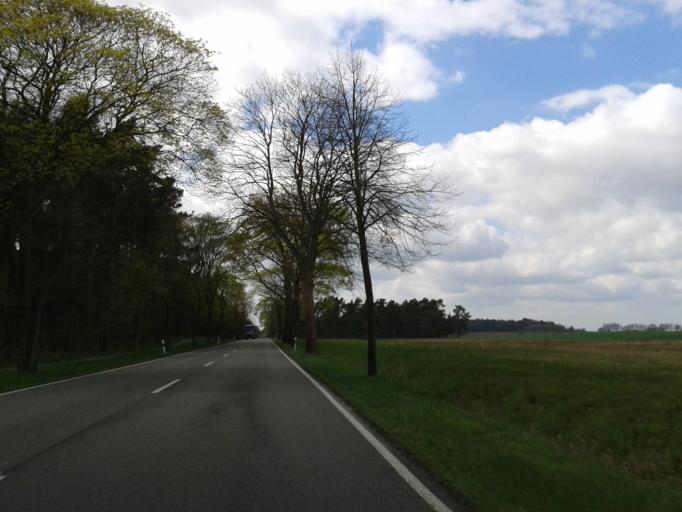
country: DE
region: Lower Saxony
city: Bergen an der Dumme
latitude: 52.8813
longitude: 11.0260
